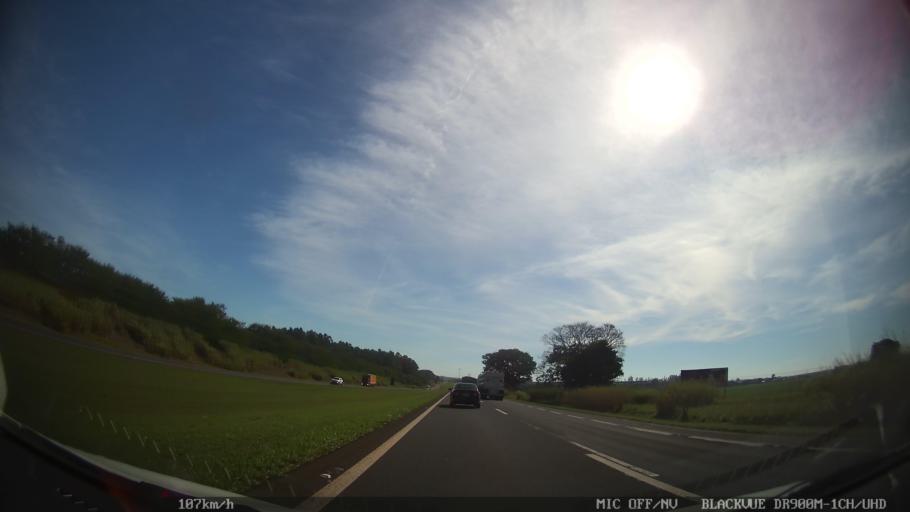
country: BR
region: Sao Paulo
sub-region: Leme
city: Leme
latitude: -22.2346
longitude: -47.3910
